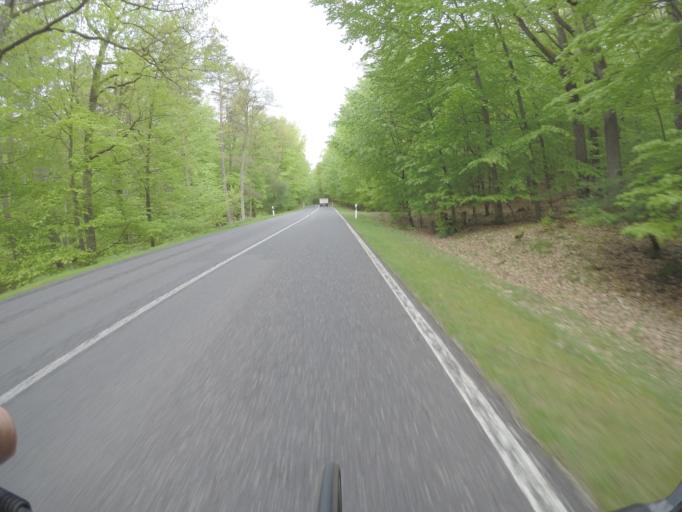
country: DE
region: Brandenburg
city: Joachimsthal
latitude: 52.9394
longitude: 13.7397
